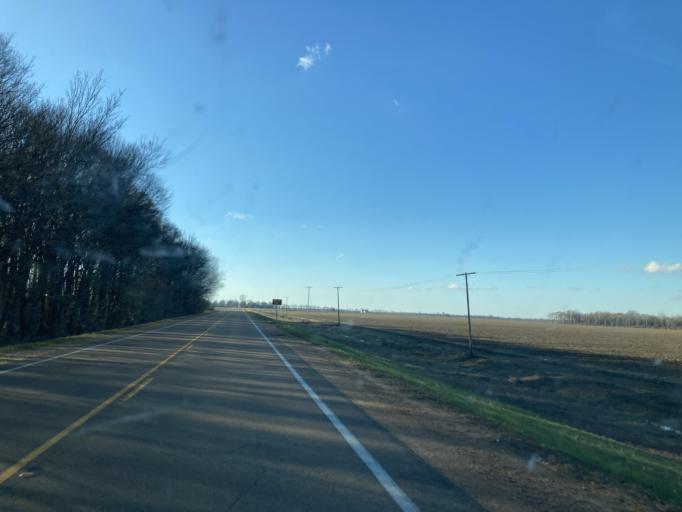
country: US
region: Mississippi
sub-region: Yazoo County
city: Yazoo City
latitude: 32.9247
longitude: -90.5714
